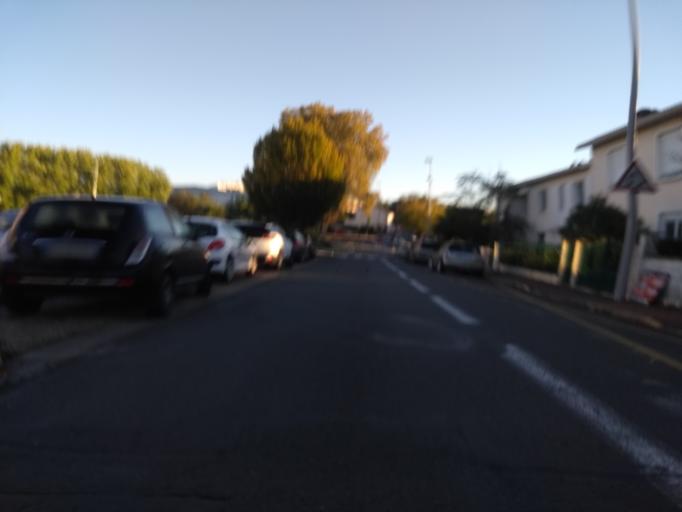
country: FR
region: Aquitaine
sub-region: Departement de la Gironde
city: Talence
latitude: 44.8083
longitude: -0.5881
